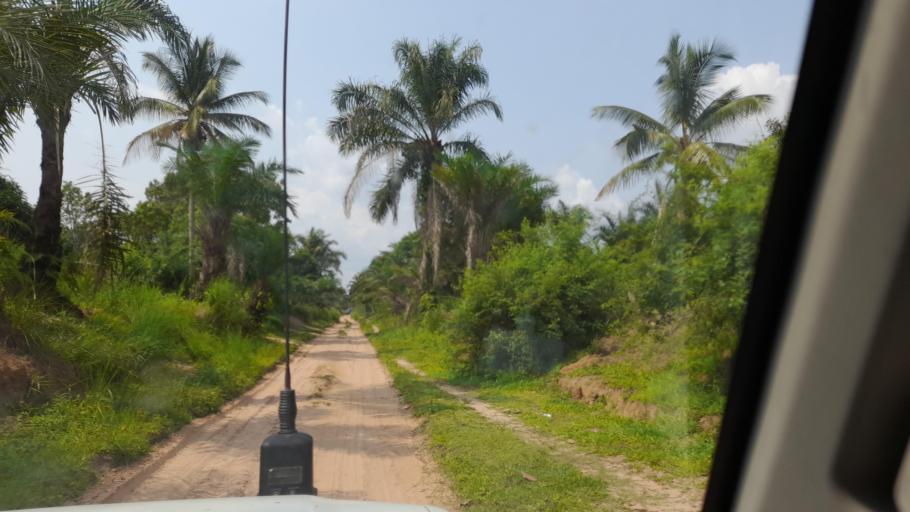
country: CD
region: Kasai-Occidental
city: Kananga
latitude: -5.9206
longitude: 22.4782
